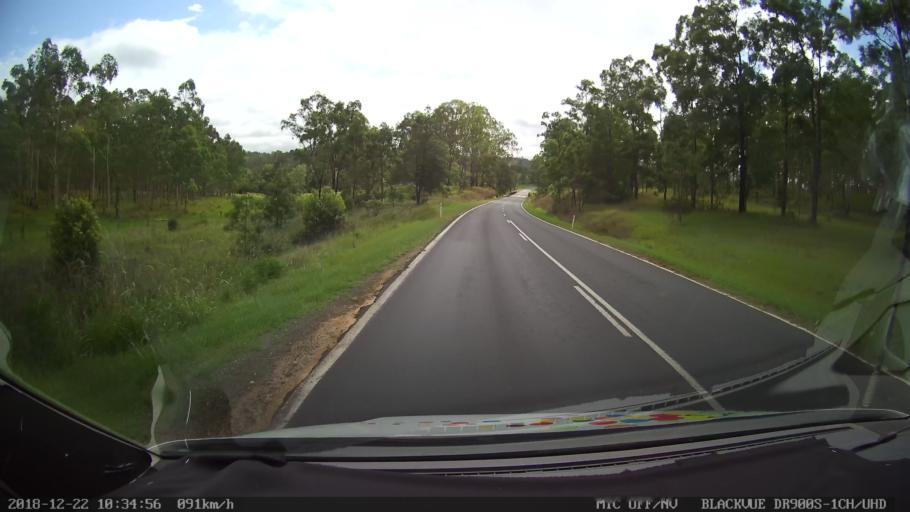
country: AU
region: New South Wales
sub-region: Clarence Valley
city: South Grafton
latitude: -29.6175
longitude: 152.6772
